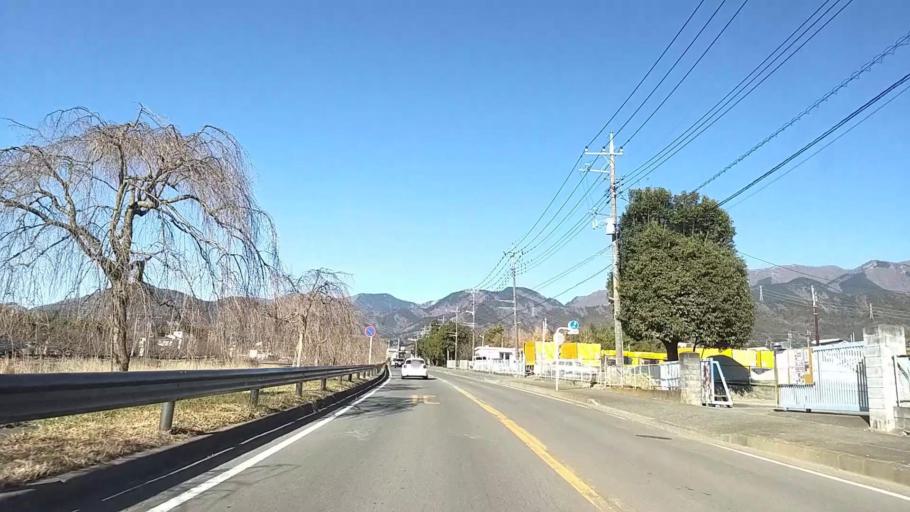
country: JP
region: Kanagawa
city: Hadano
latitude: 35.3917
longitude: 139.1842
